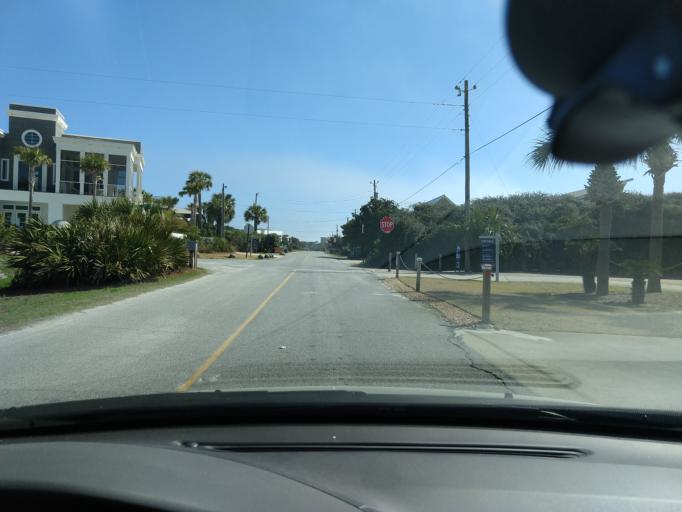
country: US
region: Florida
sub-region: Walton County
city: Seaside
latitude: 30.3377
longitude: -86.1990
